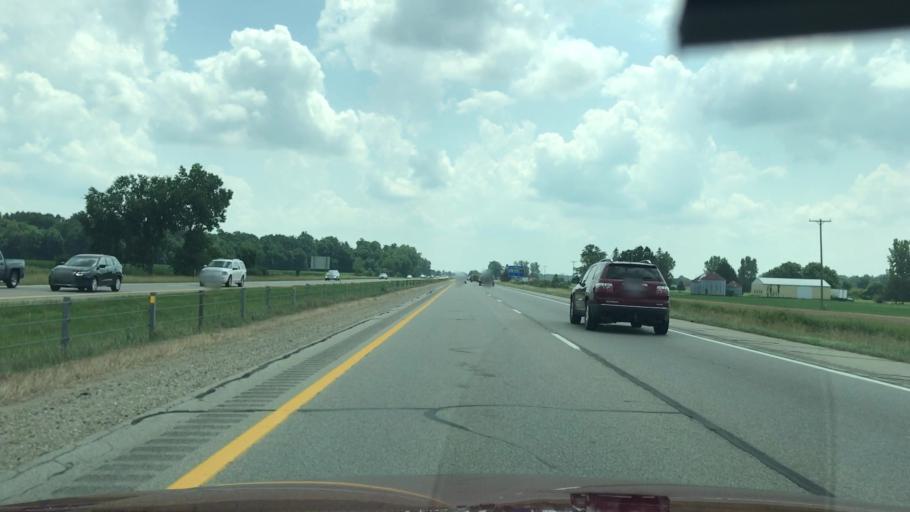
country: US
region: Michigan
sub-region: Allegan County
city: Wayland
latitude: 42.6520
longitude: -85.6622
